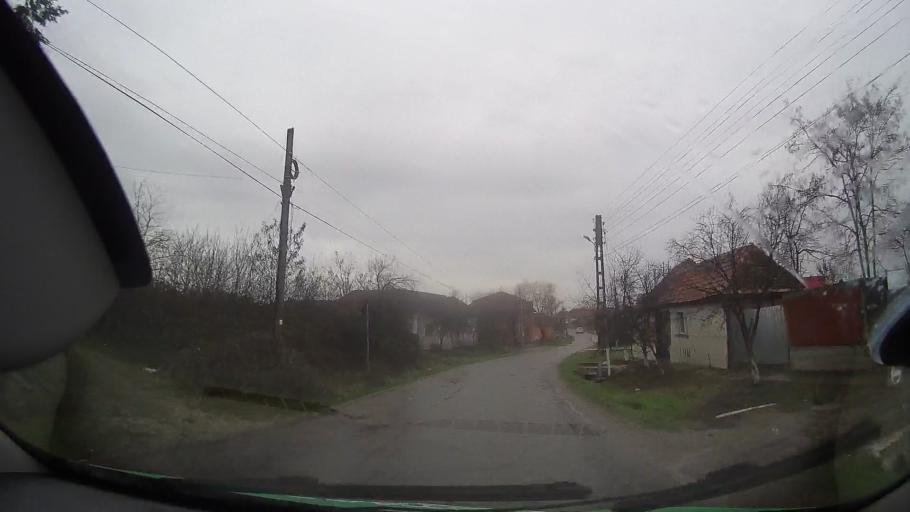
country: RO
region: Bihor
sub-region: Comuna Olcea
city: Olcea
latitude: 46.6828
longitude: 21.9723
